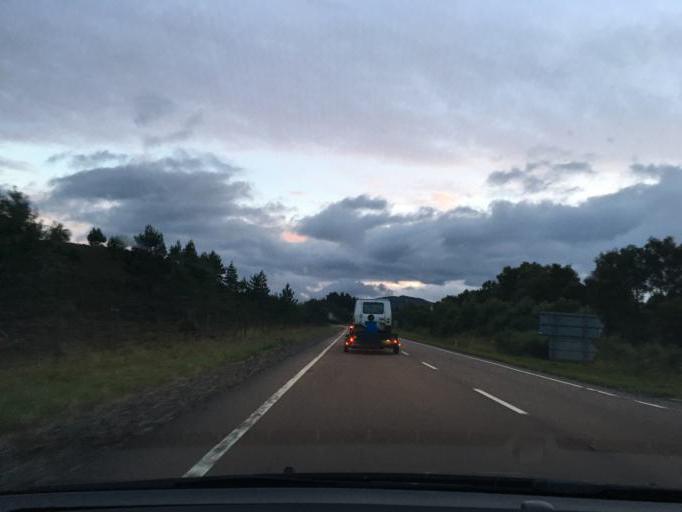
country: GB
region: Scotland
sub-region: Highland
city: Kingussie
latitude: 57.0375
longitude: -4.1524
